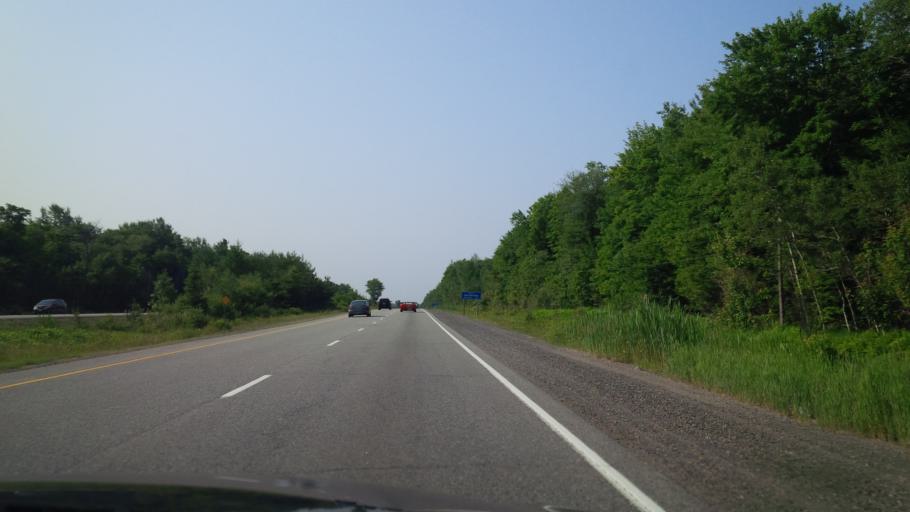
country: CA
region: Ontario
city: Bracebridge
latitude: 45.1552
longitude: -79.3118
